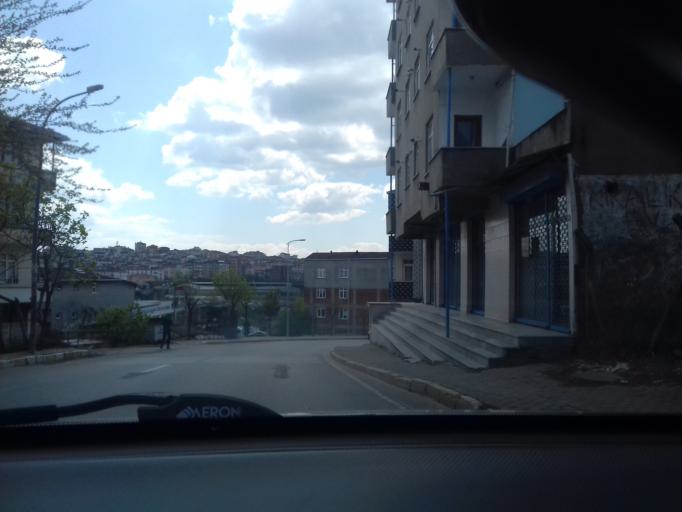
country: TR
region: Istanbul
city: Pendik
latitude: 40.8707
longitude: 29.2808
